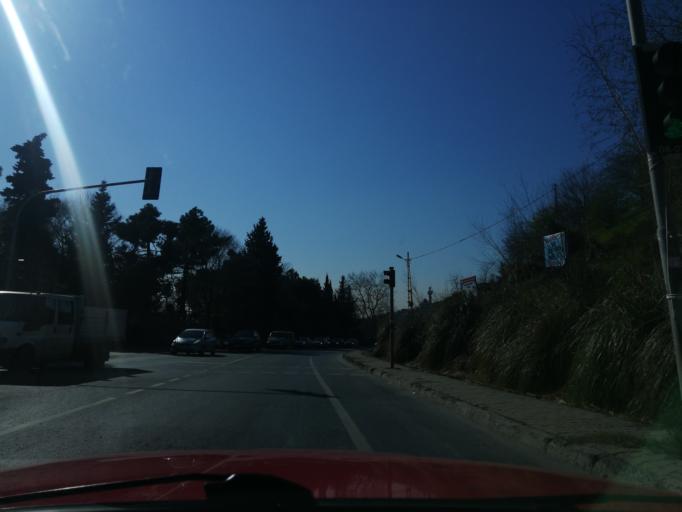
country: TR
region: Istanbul
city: Mahmut Sevket Pasa
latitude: 41.1211
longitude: 29.1356
